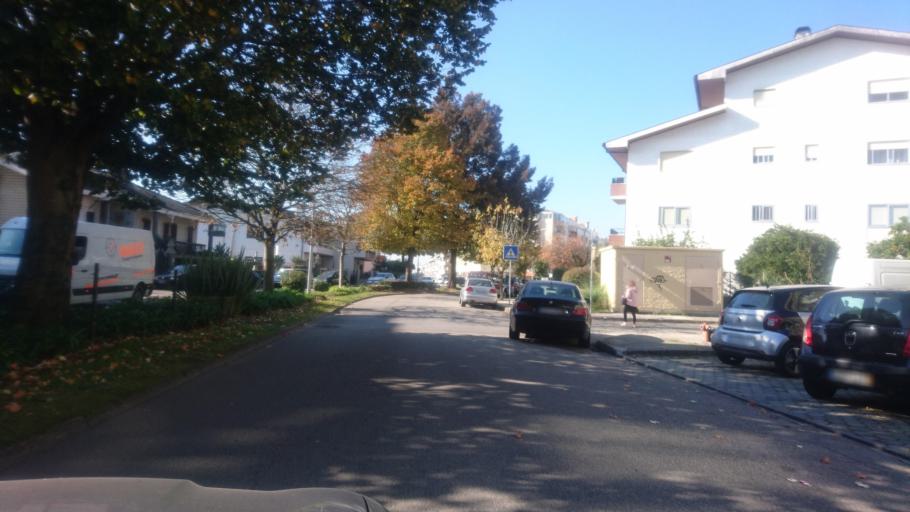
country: PT
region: Aveiro
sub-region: Santa Maria da Feira
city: Feira
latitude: 40.9243
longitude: -8.5596
